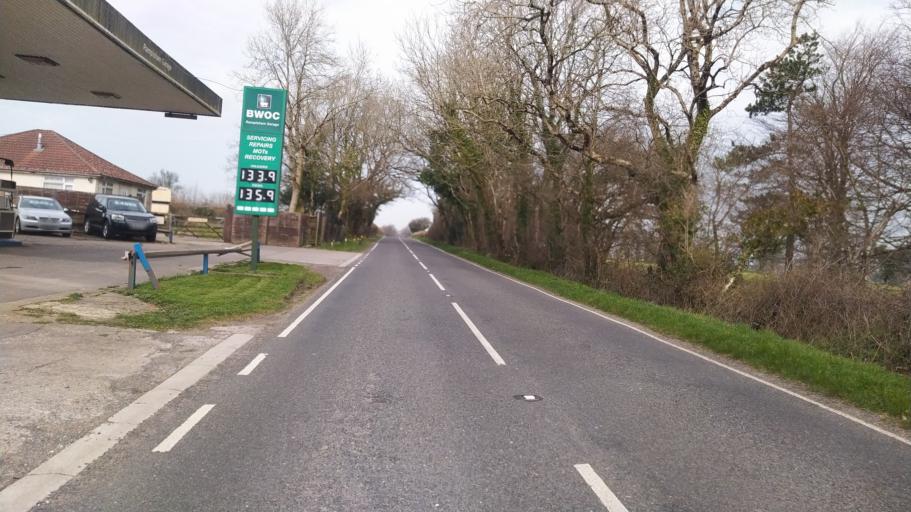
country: GB
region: England
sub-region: Dorset
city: Beaminster
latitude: 50.8152
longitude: -2.6551
